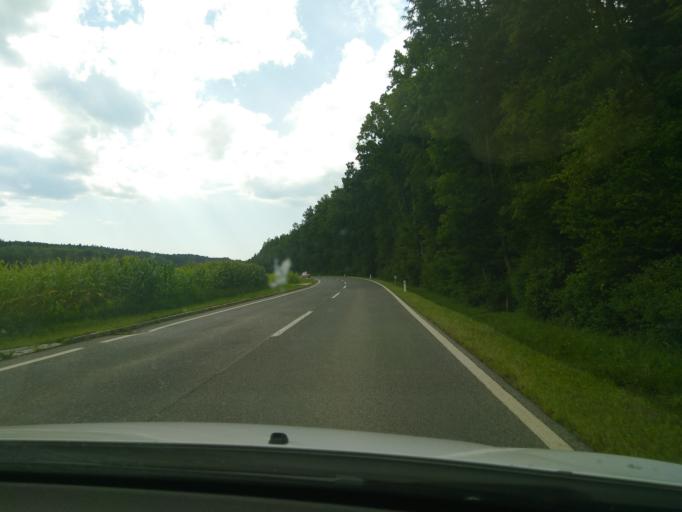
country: AT
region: Burgenland
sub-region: Politischer Bezirk Oberwart
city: Oberschutzen
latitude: 47.3509
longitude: 16.1713
